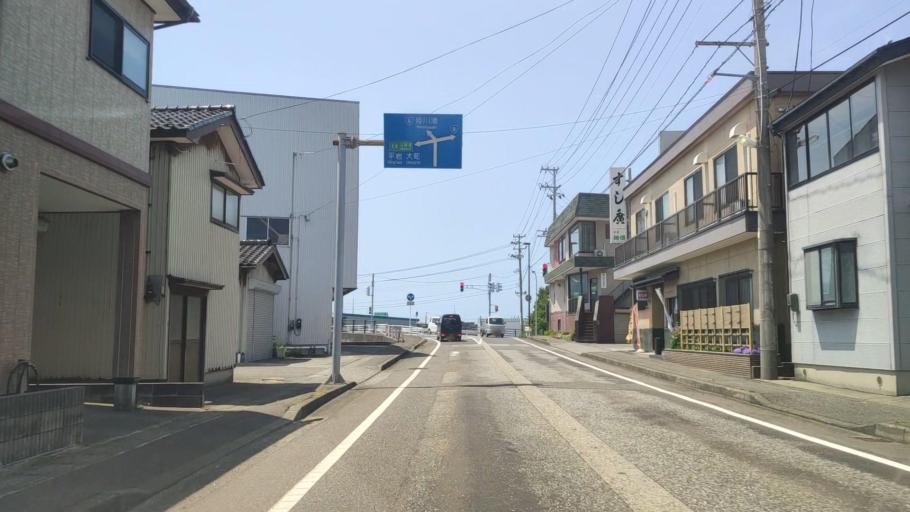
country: JP
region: Niigata
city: Itoigawa
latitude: 37.0422
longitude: 137.8524
